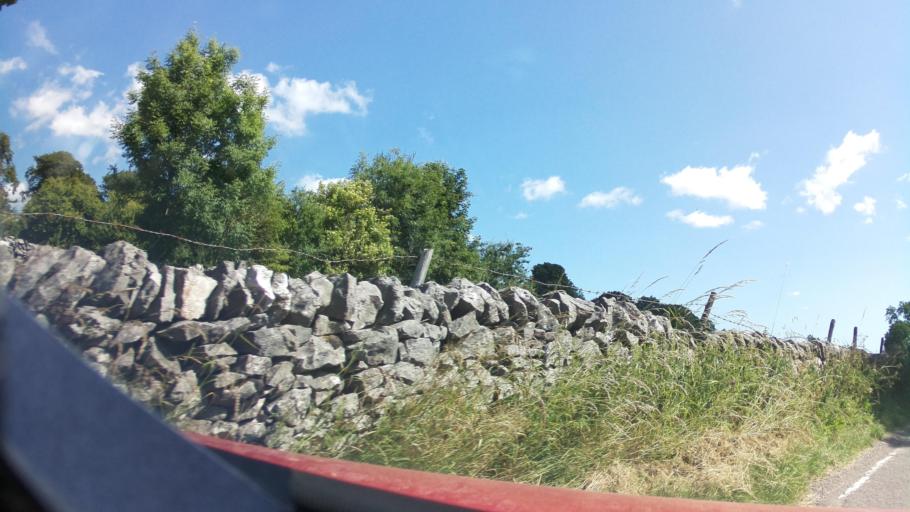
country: GB
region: England
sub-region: Derbyshire
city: Tideswell
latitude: 53.2618
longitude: -1.8140
